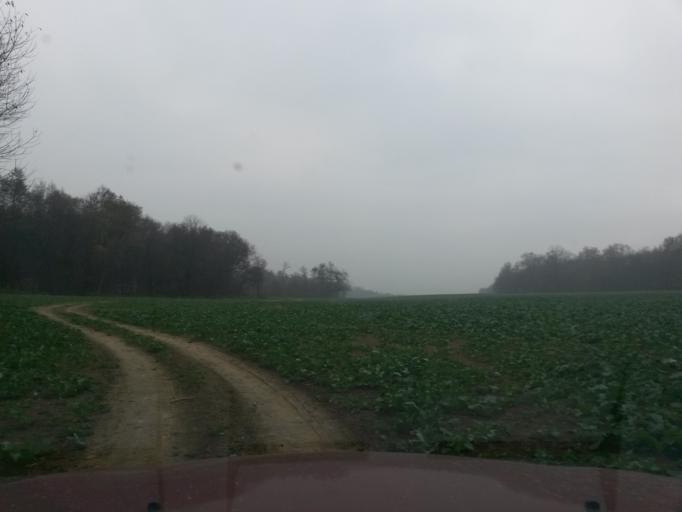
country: SK
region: Presovsky
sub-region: Okres Presov
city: Presov
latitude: 48.8915
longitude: 21.2958
